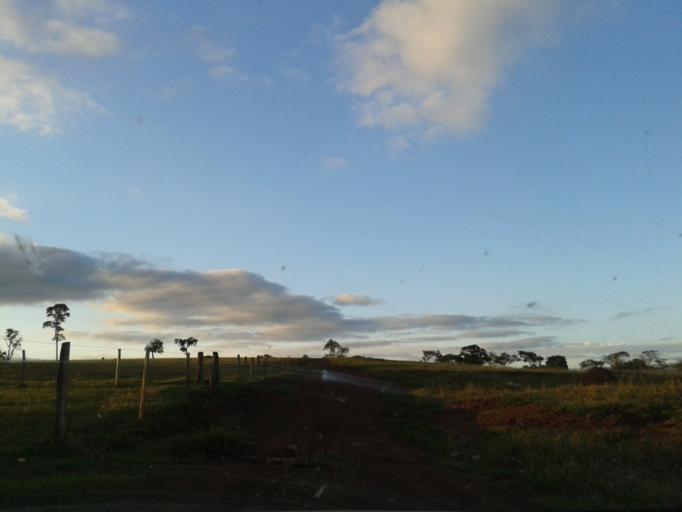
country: BR
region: Minas Gerais
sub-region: Campina Verde
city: Campina Verde
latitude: -19.4964
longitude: -49.6790
